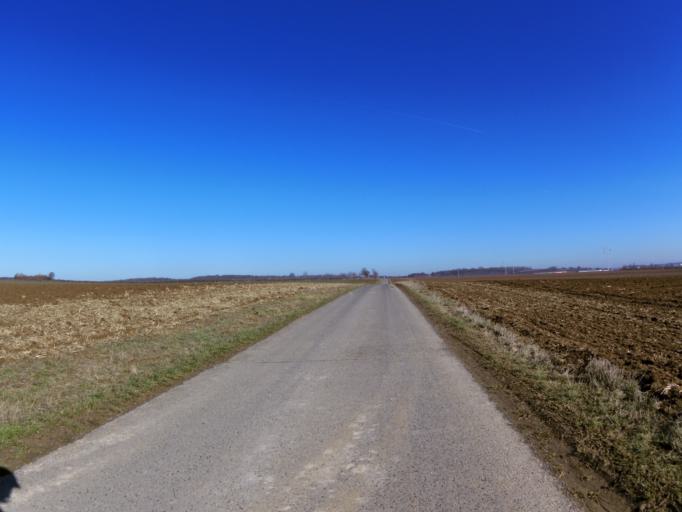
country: DE
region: Bavaria
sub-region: Regierungsbezirk Unterfranken
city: Estenfeld
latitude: 49.8395
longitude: 9.9941
